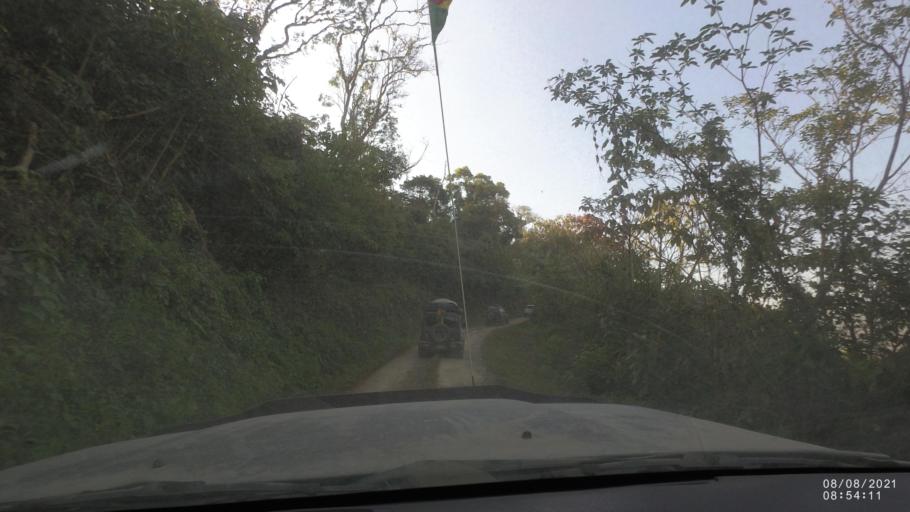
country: BO
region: La Paz
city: Quime
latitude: -16.5421
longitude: -66.7521
